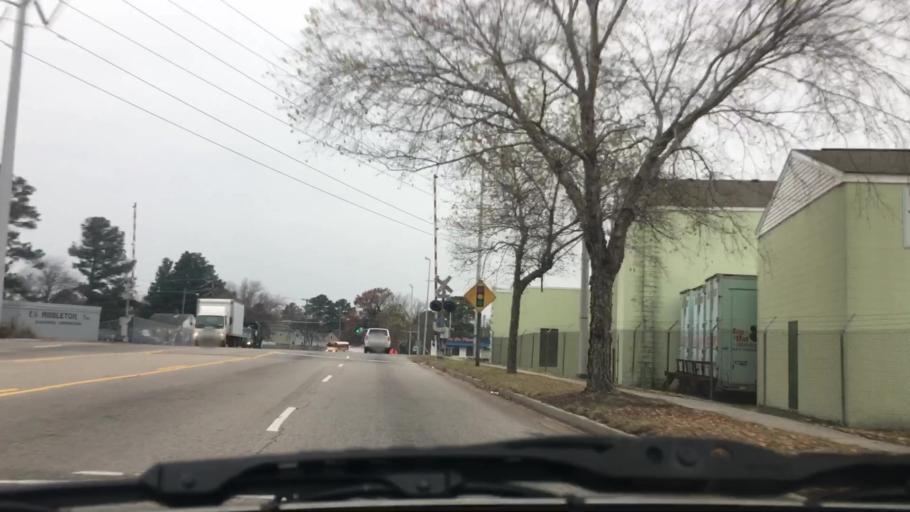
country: US
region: Virginia
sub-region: City of Norfolk
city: Norfolk
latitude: 36.8669
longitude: -76.2485
